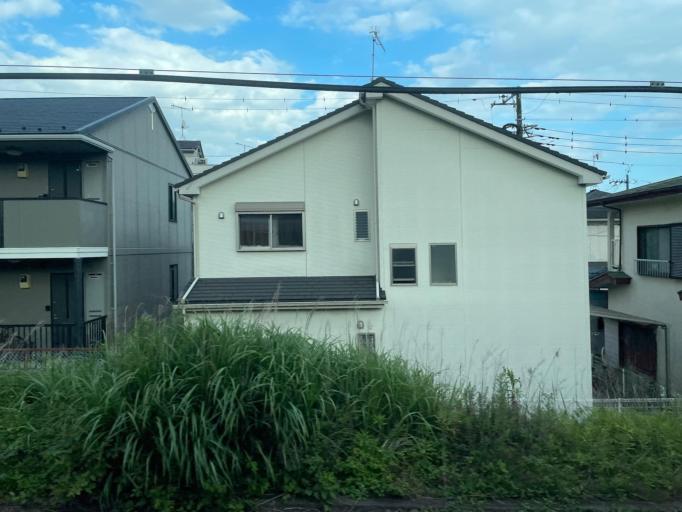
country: JP
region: Kanagawa
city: Isehara
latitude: 35.3754
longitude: 139.2731
